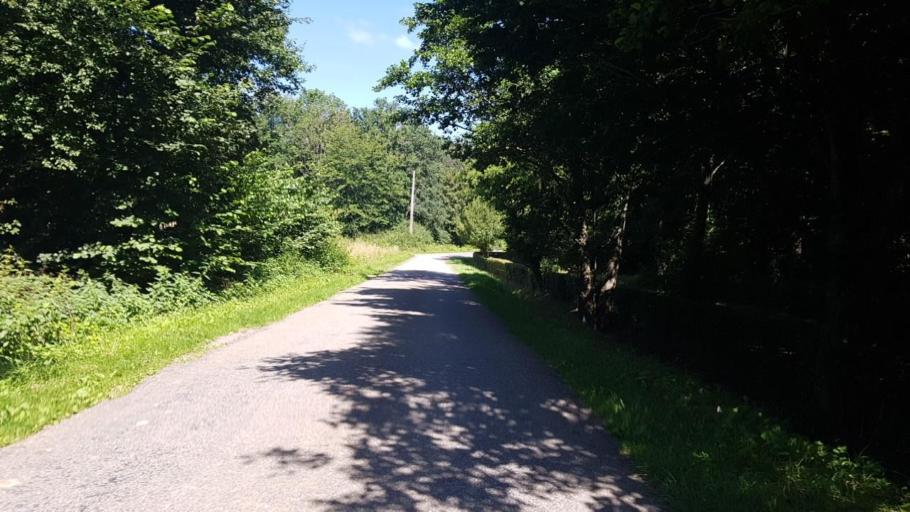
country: BE
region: Wallonia
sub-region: Province du Hainaut
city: Momignies
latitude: 50.0745
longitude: 4.2315
